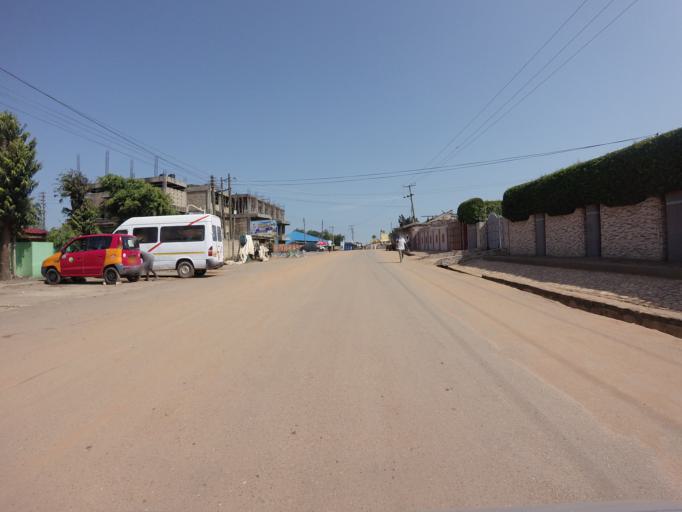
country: GH
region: Greater Accra
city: Dome
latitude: 5.6347
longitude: -0.2333
